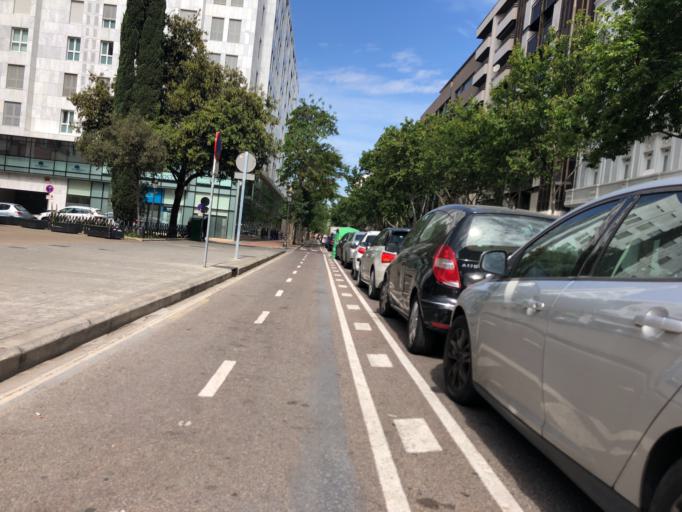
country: ES
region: Valencia
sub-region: Provincia de Valencia
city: Valencia
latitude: 39.4746
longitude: -0.3596
